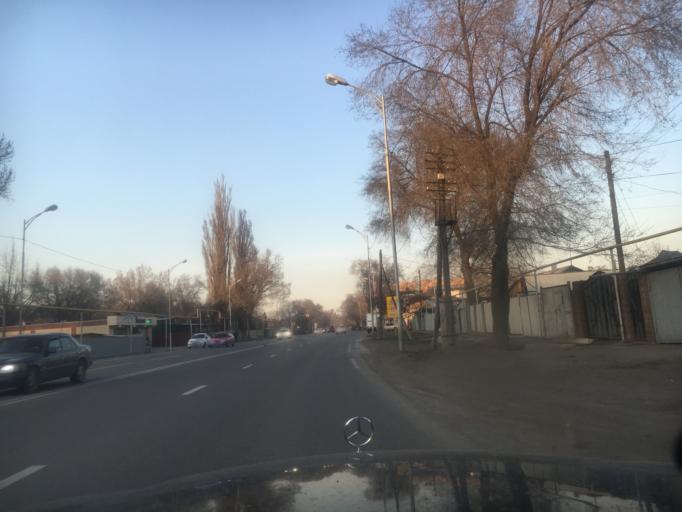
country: KZ
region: Almaty Oblysy
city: Pervomayskiy
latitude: 43.3567
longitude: 76.9780
